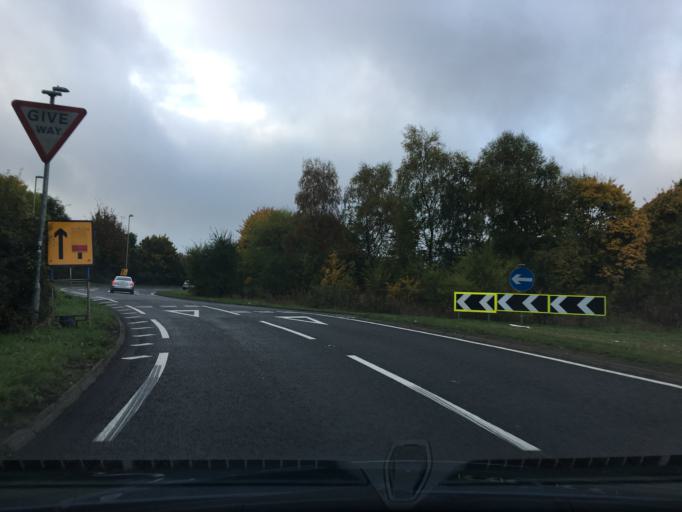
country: GB
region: England
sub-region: Hampshire
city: Alton
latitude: 51.1576
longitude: -0.9491
